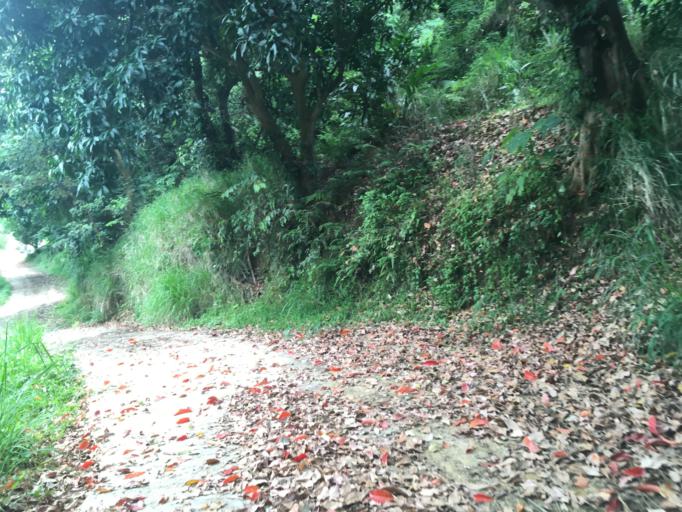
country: TW
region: Taiwan
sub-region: Hsinchu
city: Hsinchu
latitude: 24.7436
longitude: 120.9783
